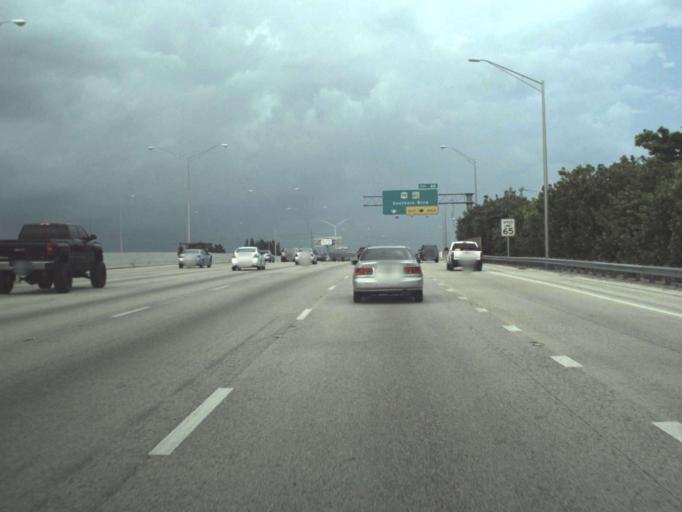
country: US
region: Florida
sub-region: Palm Beach County
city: Lake Clarke Shores
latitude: 26.6645
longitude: -80.0707
